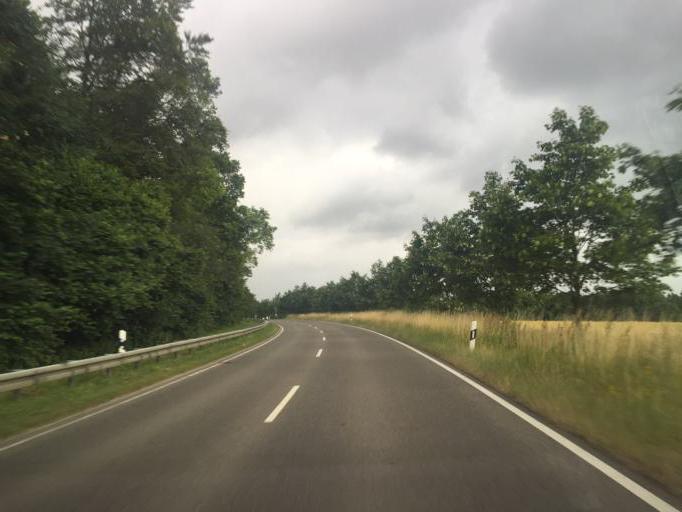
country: DE
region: Baden-Wuerttemberg
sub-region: Regierungsbezirk Stuttgart
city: Nufringen
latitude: 48.6458
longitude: 8.8650
